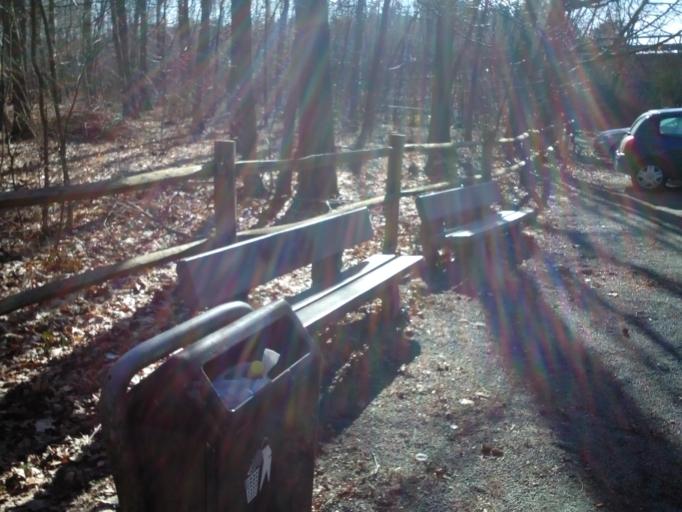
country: BE
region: Flanders
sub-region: Provincie Vlaams-Brabant
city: Leuven
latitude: 50.8462
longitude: 4.7037
